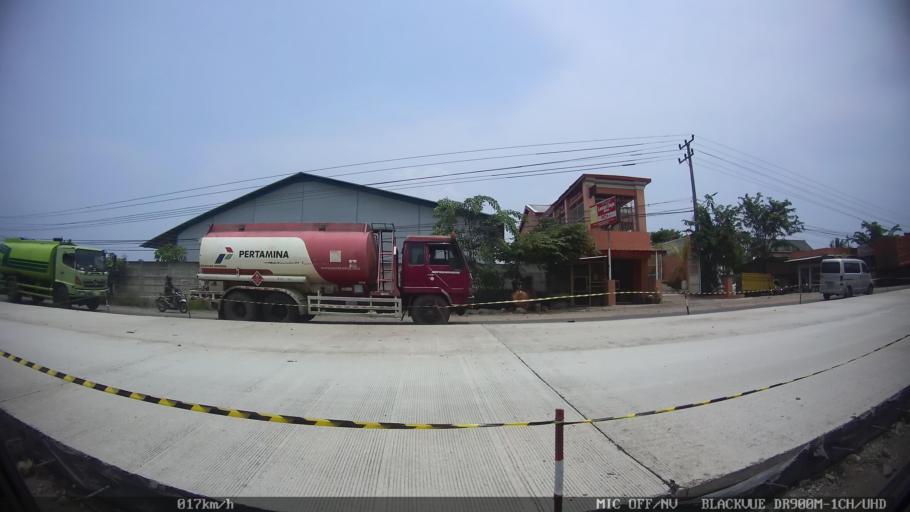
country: ID
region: Lampung
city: Kedaton
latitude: -5.4028
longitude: 105.2904
